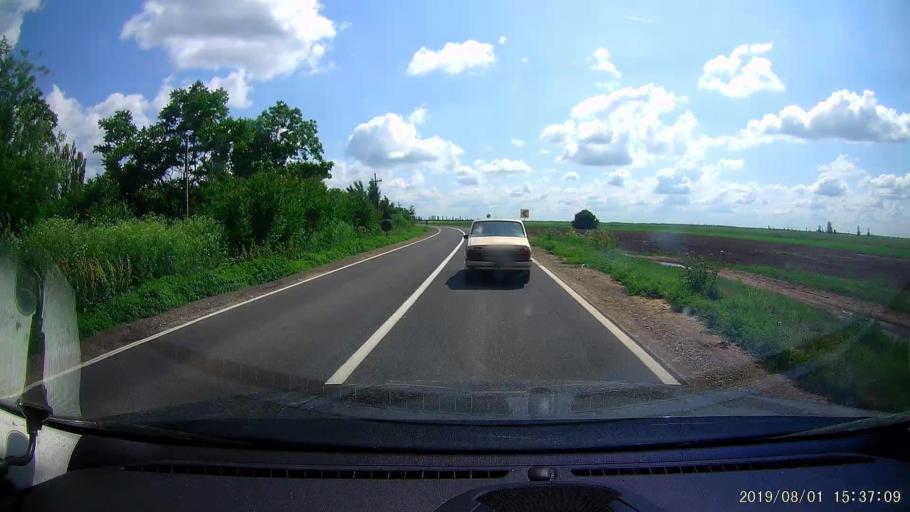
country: RO
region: Braila
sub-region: Comuna Insuratei
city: Insuratei
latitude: 44.9048
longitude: 27.5905
